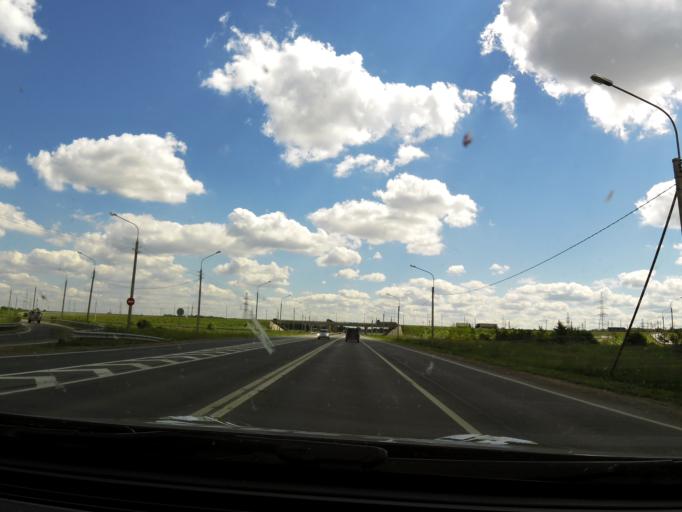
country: RU
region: Vologda
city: Molochnoye
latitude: 59.2499
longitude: 39.7709
